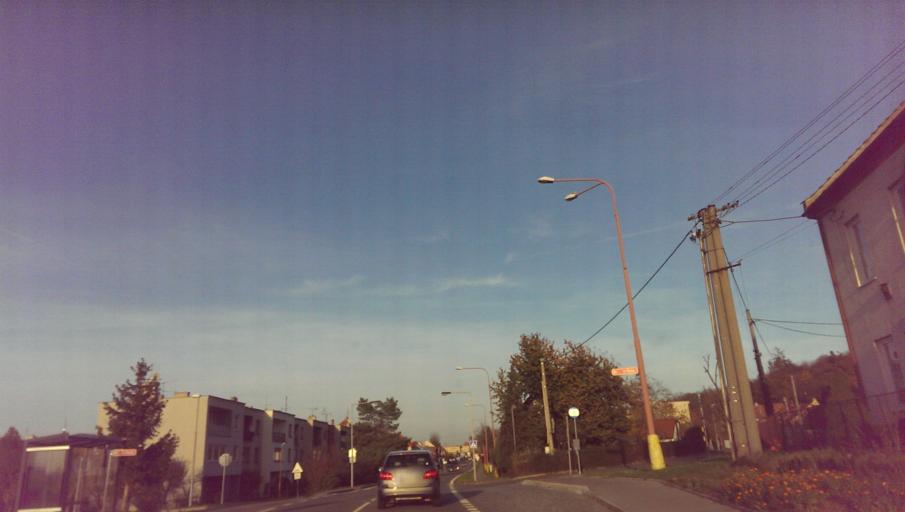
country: CZ
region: Zlin
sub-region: Okres Uherske Hradiste
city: Uherske Hradiste
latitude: 49.0819
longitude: 17.4891
